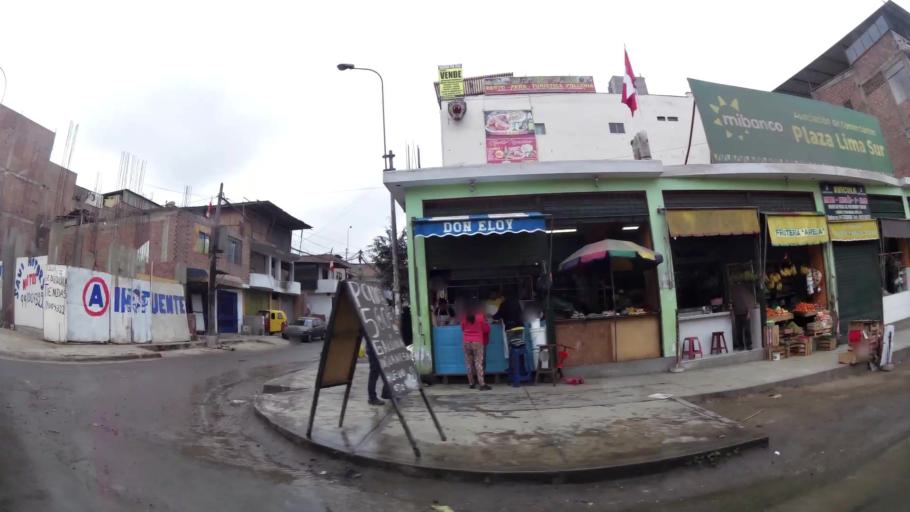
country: PE
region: Lima
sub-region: Lima
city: Surco
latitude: -12.1468
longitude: -76.9677
